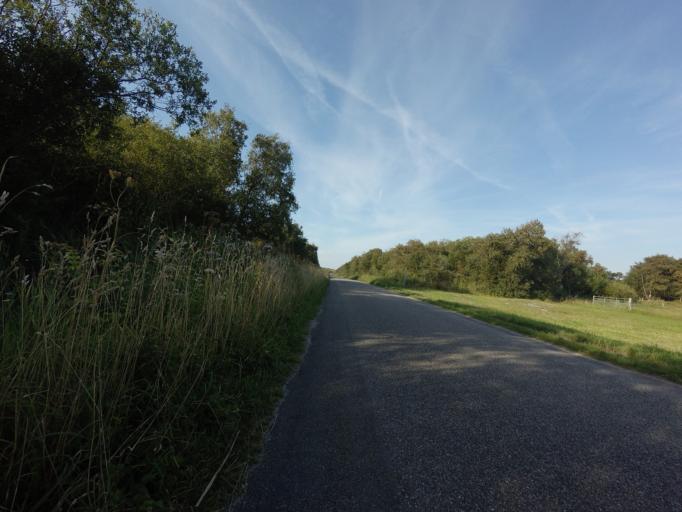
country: NL
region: Friesland
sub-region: Gemeente Schiermonnikoog
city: Schiermonnikoog
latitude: 53.4933
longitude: 6.1849
